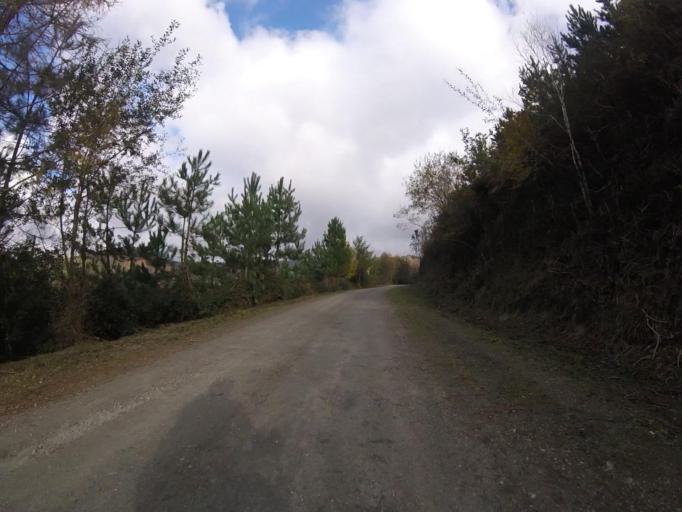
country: ES
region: Navarre
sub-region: Provincia de Navarra
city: Goizueta
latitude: 43.2208
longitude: -1.8435
